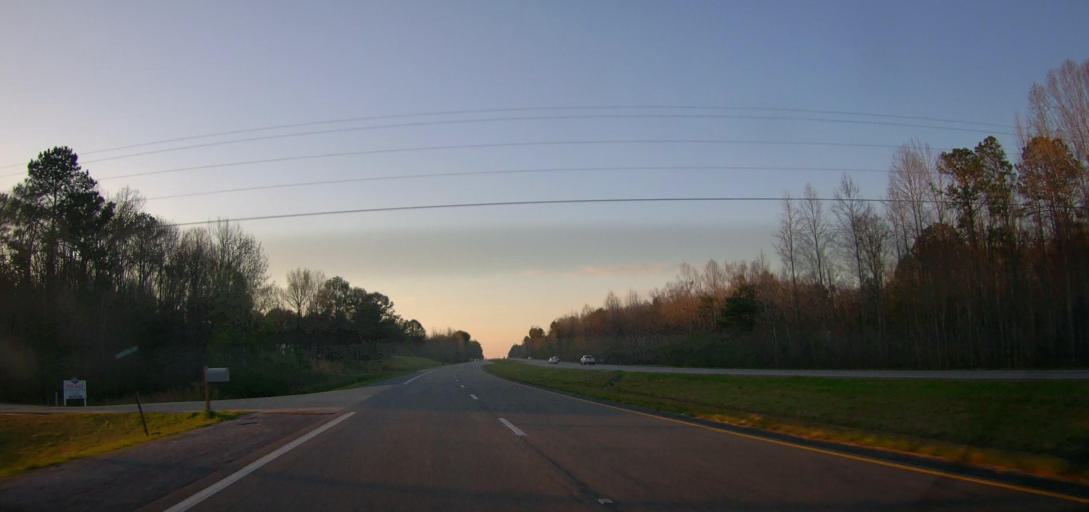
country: US
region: Alabama
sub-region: Coosa County
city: Stewartville
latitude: 33.1162
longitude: -86.2389
